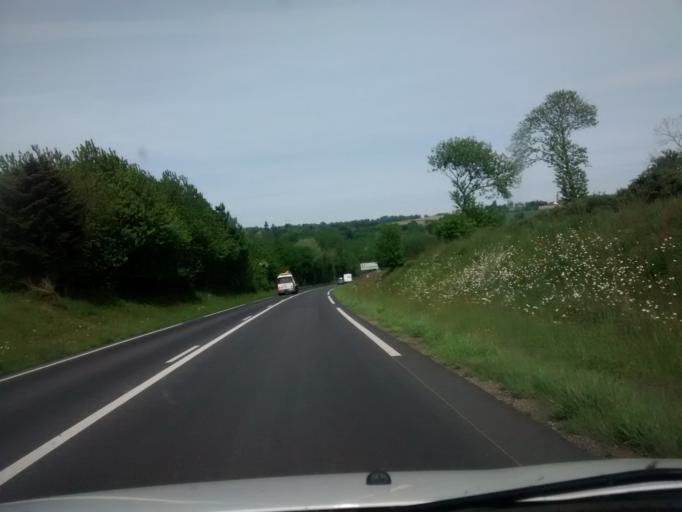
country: FR
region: Brittany
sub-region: Departement d'Ille-et-Vilaine
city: Antrain
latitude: 48.4555
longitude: -1.4888
